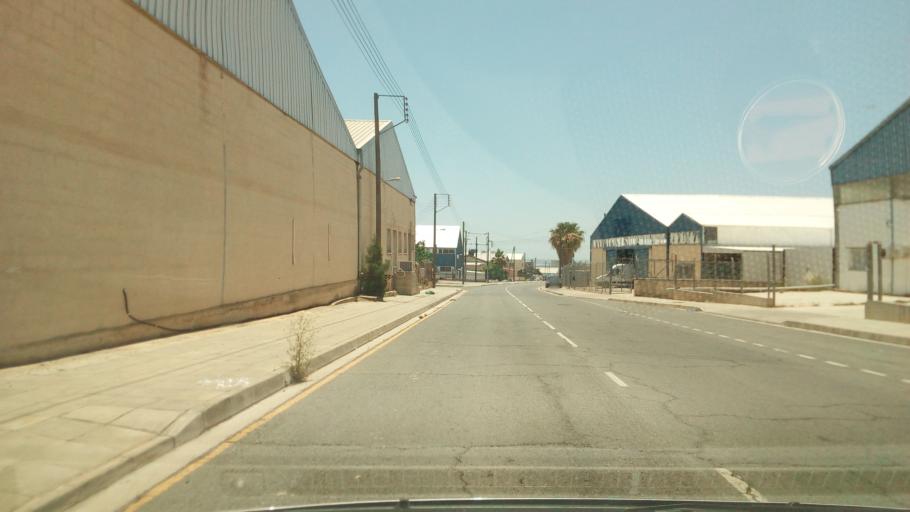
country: CY
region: Limassol
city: Ypsonas
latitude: 34.7046
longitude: 32.9557
